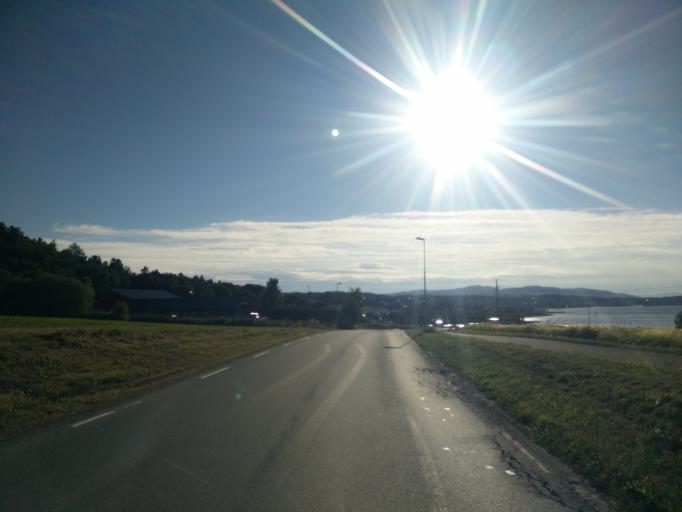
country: NO
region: Sor-Trondelag
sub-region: Malvik
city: Malvik
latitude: 63.4310
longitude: 10.5723
